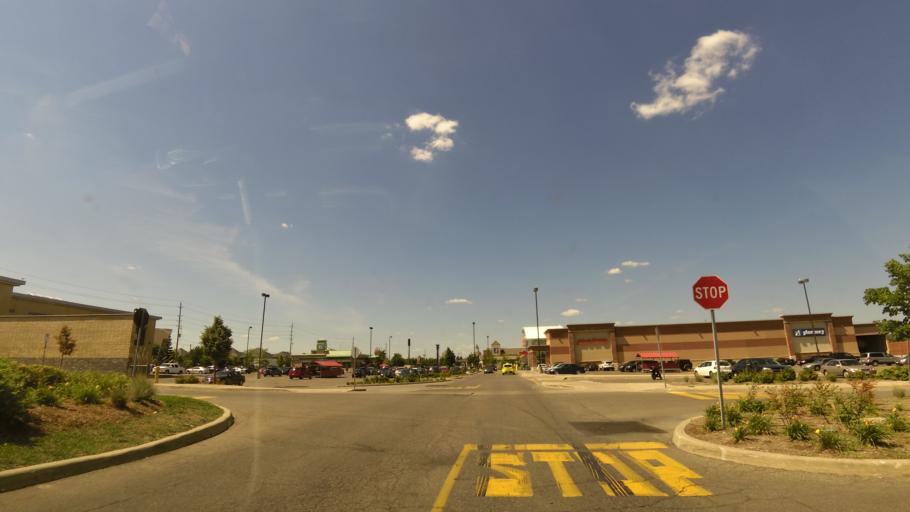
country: CA
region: Ontario
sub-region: Halton
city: Milton
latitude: 43.6313
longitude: -79.8762
